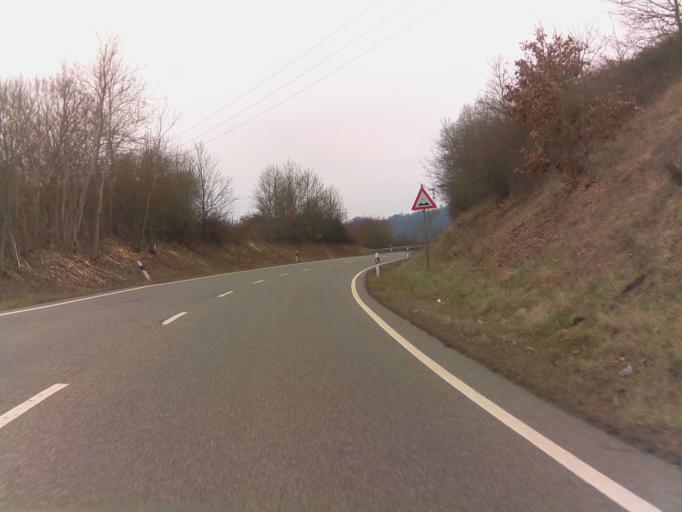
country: DE
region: Rheinland-Pfalz
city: Oberndorf
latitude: 49.7298
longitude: 7.8139
